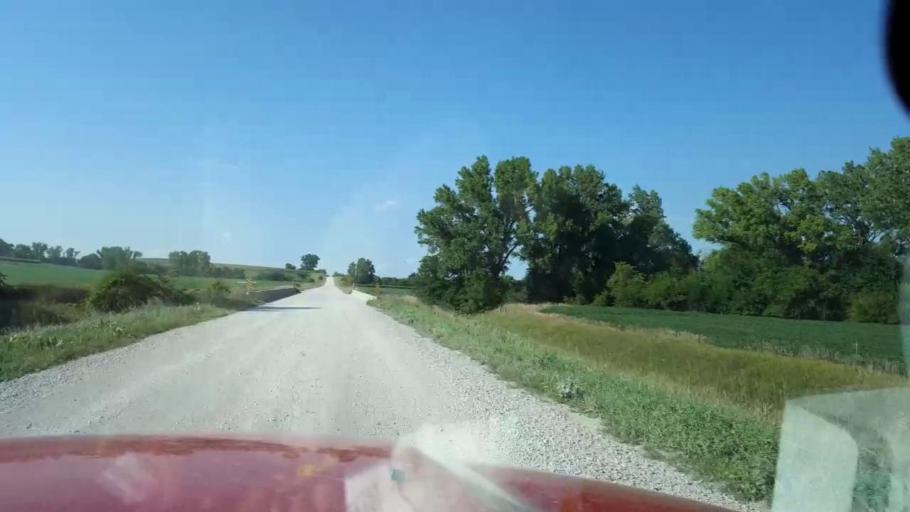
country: US
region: Iowa
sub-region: Pottawattamie County
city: Oakland
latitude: 41.2485
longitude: -95.5371
